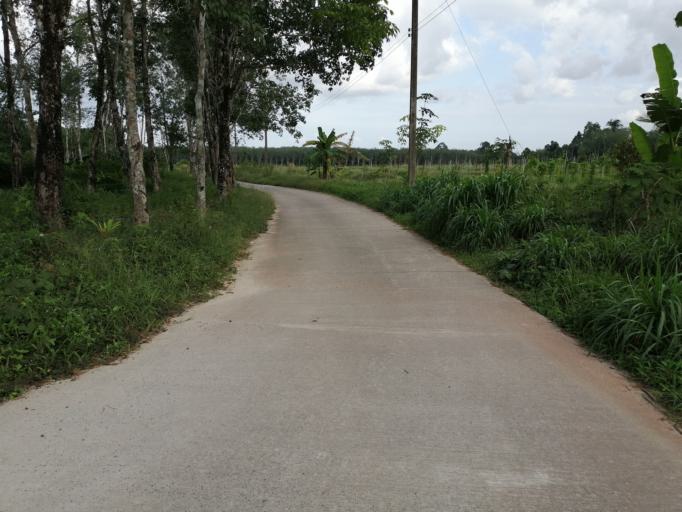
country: TH
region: Nakhon Si Thammarat
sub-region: Amphoe Nopphitam
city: Nopphitam
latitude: 8.6989
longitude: 99.7479
